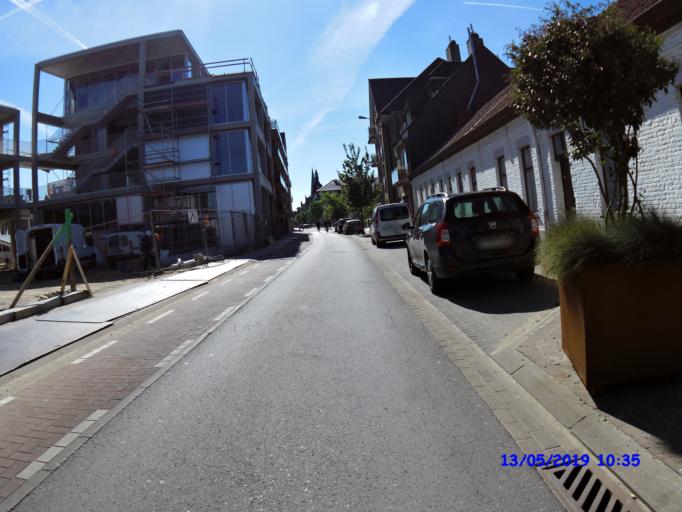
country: BE
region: Flanders
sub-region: Provincie West-Vlaanderen
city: Waregem
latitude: 50.8892
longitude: 3.4270
